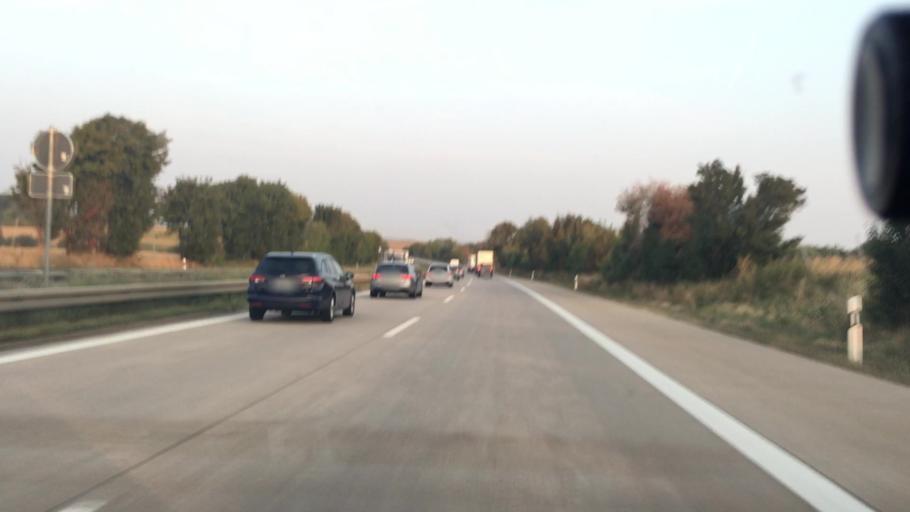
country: DE
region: Saxony
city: Nerchau
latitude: 51.2514
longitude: 12.8382
